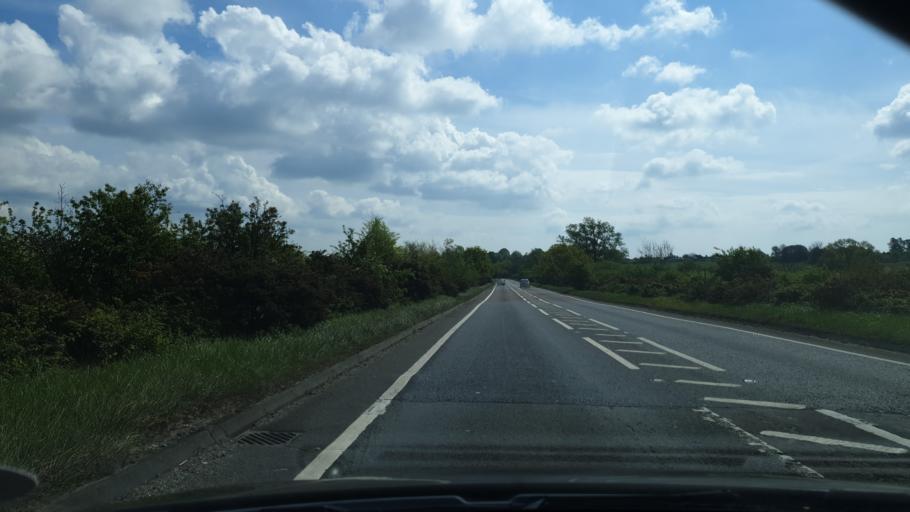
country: GB
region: England
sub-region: Suffolk
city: Shotley Gate
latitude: 51.9352
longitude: 1.2368
